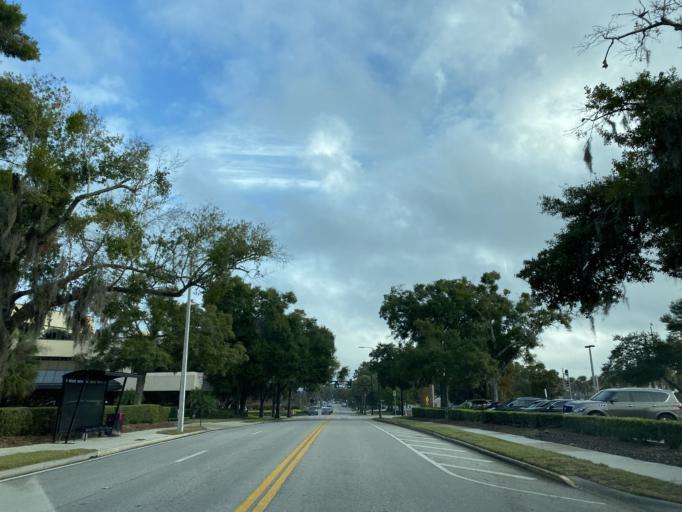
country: US
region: Florida
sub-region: Orange County
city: Orlando
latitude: 28.5590
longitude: -81.3779
